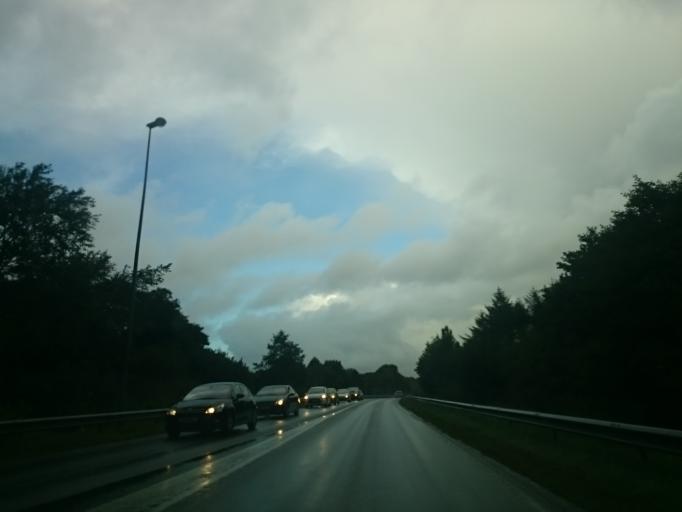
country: FR
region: Brittany
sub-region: Departement du Finistere
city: Gouesnou
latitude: 48.4446
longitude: -4.4557
